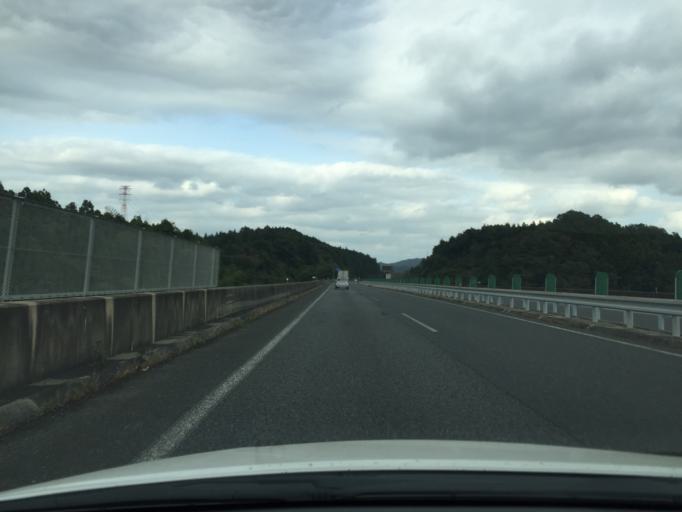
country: JP
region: Ibaraki
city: Kitaibaraki
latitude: 36.9059
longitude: 140.7515
